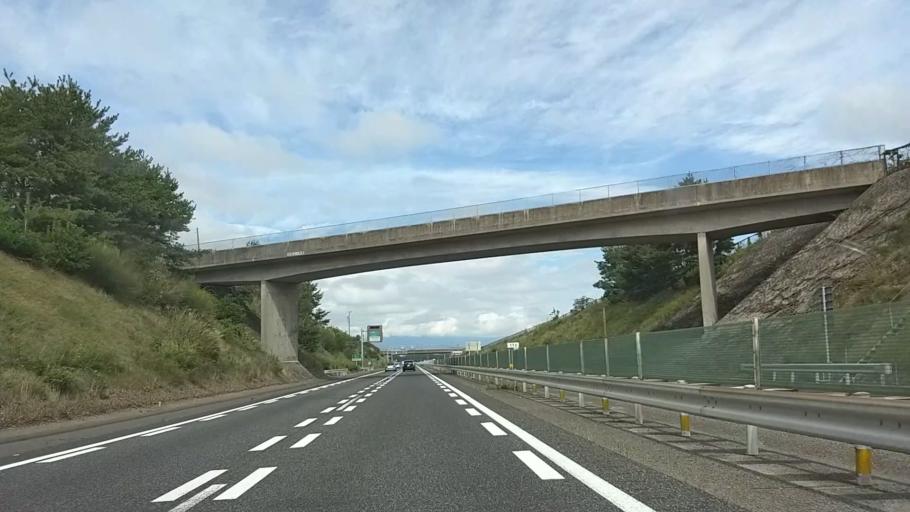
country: JP
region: Nagano
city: Shiojiri
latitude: 36.1238
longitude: 137.9779
